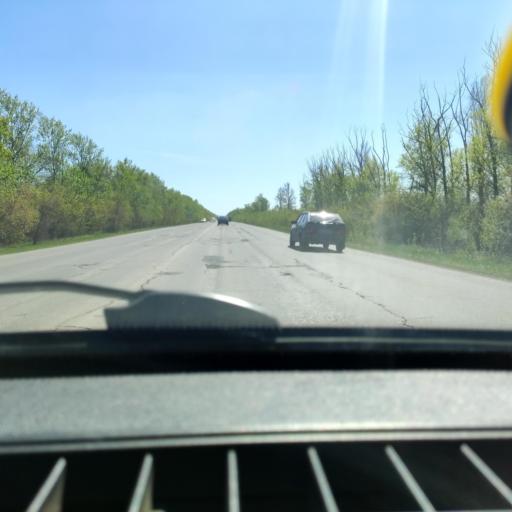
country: RU
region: Samara
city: Tol'yatti
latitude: 53.6132
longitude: 49.4125
